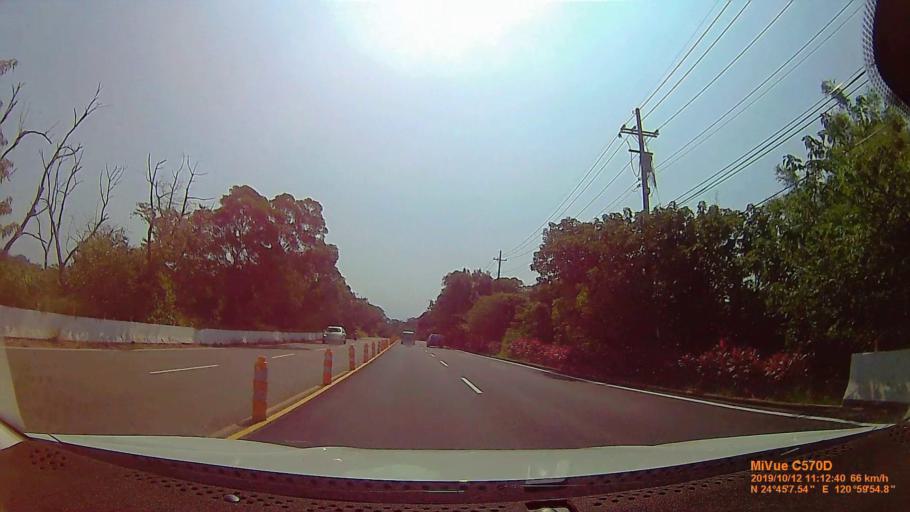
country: TW
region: Taiwan
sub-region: Hsinchu
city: Hsinchu
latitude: 24.7521
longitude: 120.9987
